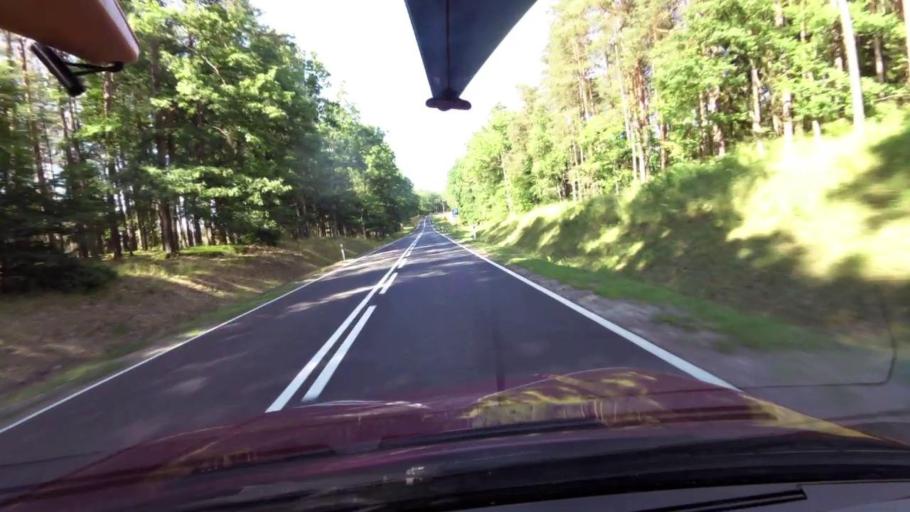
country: PL
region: Pomeranian Voivodeship
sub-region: Powiat bytowski
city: Trzebielino
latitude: 54.1242
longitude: 17.0057
